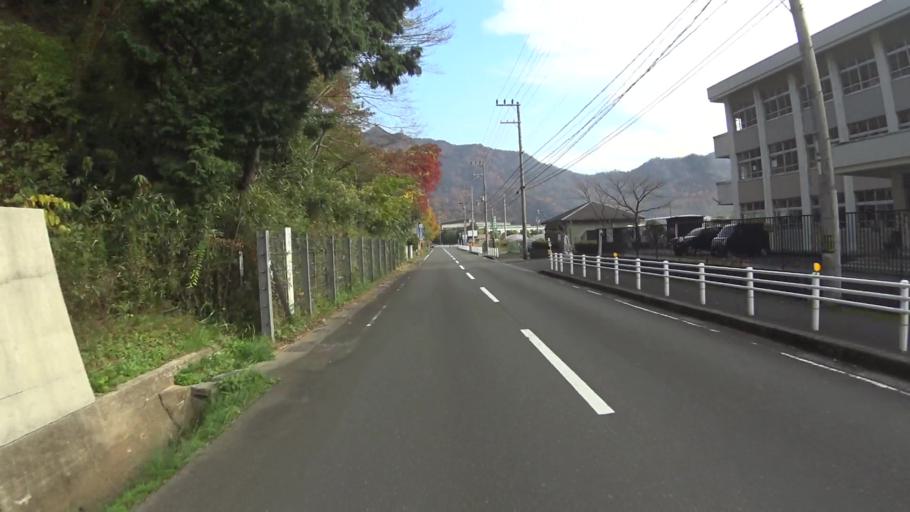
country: JP
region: Kyoto
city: Maizuru
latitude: 35.5182
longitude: 135.3957
